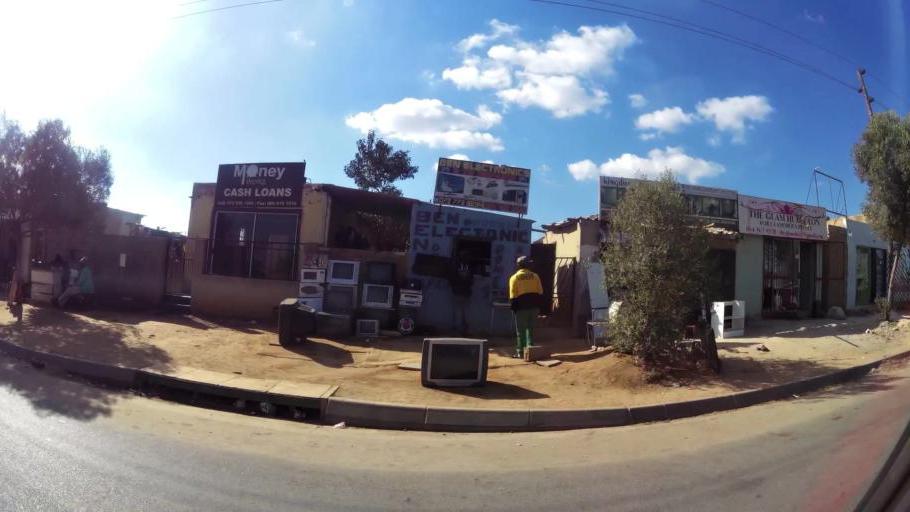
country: ZA
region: Gauteng
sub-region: West Rand District Municipality
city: Muldersdriseloop
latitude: -26.0243
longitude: 27.9240
